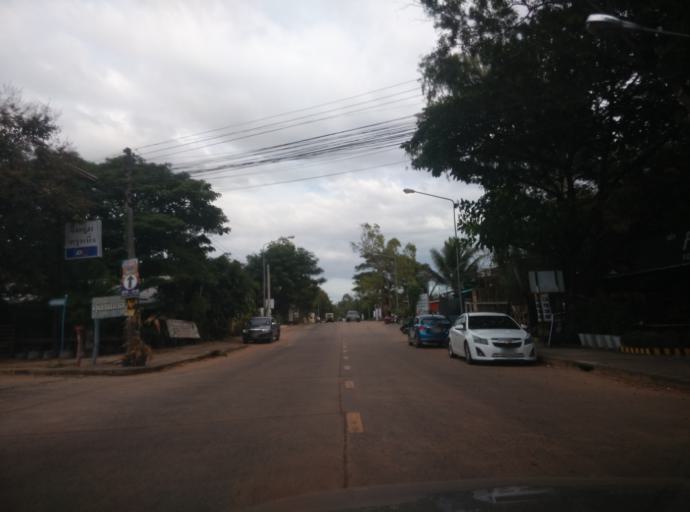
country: TH
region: Sisaket
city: Si Sa Ket
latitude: 15.1221
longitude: 104.3396
